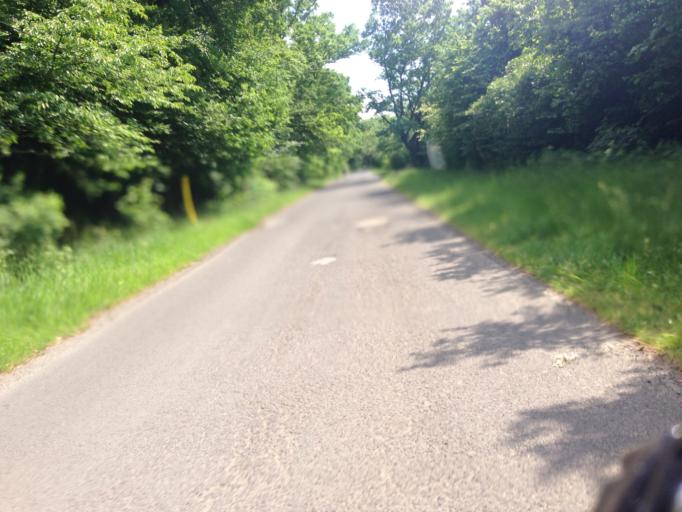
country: DE
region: Hesse
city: Obertshausen
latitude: 50.0655
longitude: 8.8847
